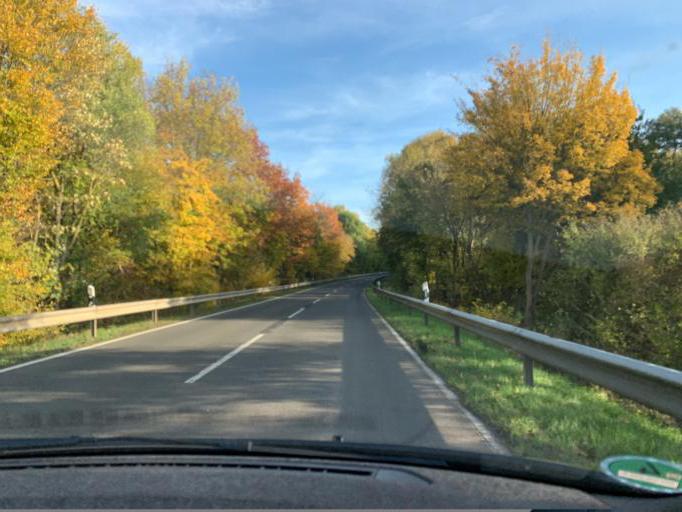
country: DE
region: North Rhine-Westphalia
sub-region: Regierungsbezirk Koln
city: Kreuzau
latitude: 50.7217
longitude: 6.5141
